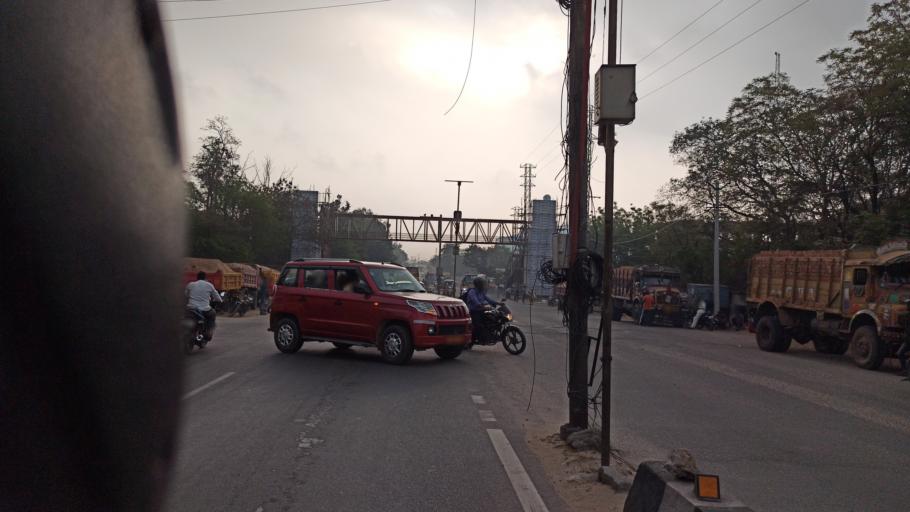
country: IN
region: Telangana
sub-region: Rangareddi
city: Uppal Kalan
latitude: 17.4013
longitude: 78.5490
